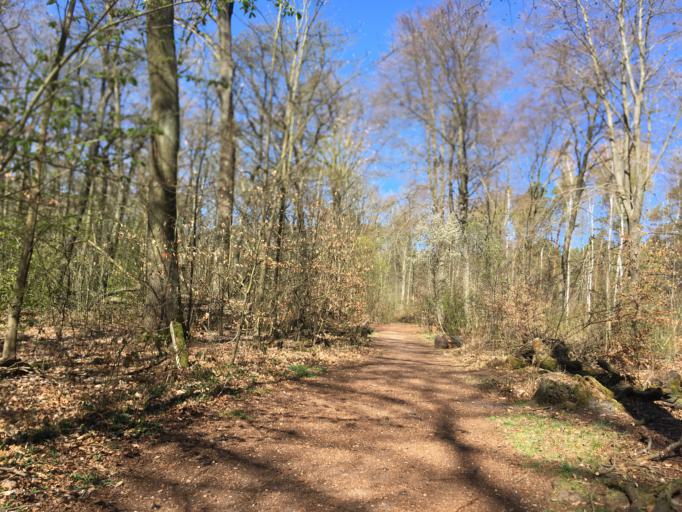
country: DE
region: Brandenburg
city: Wandlitz
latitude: 52.6901
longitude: 13.4696
